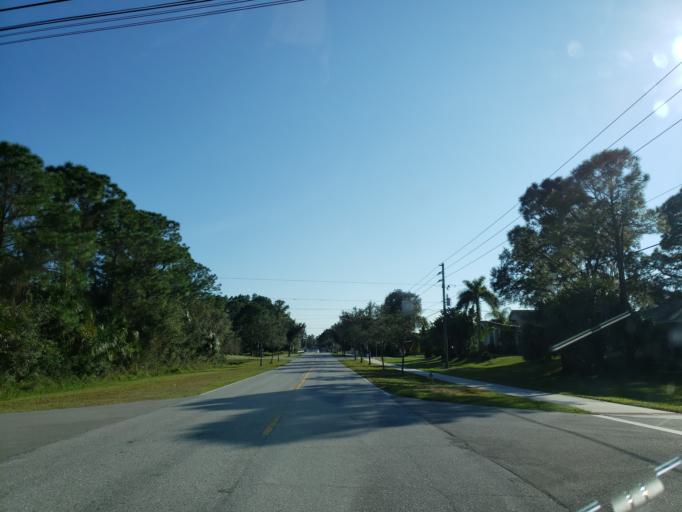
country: US
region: Florida
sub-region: Sarasota County
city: North Port
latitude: 27.0781
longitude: -82.1952
